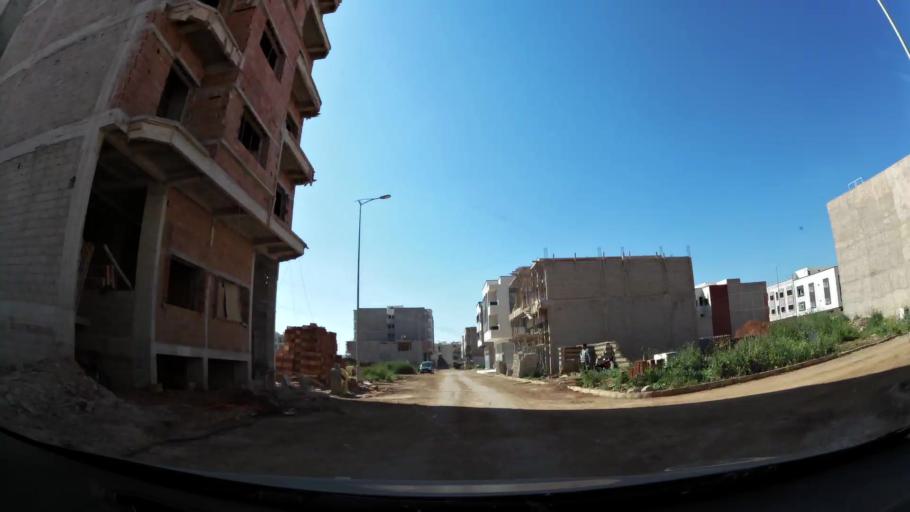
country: MA
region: Fes-Boulemane
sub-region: Fes
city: Fes
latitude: 33.9933
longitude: -5.0094
